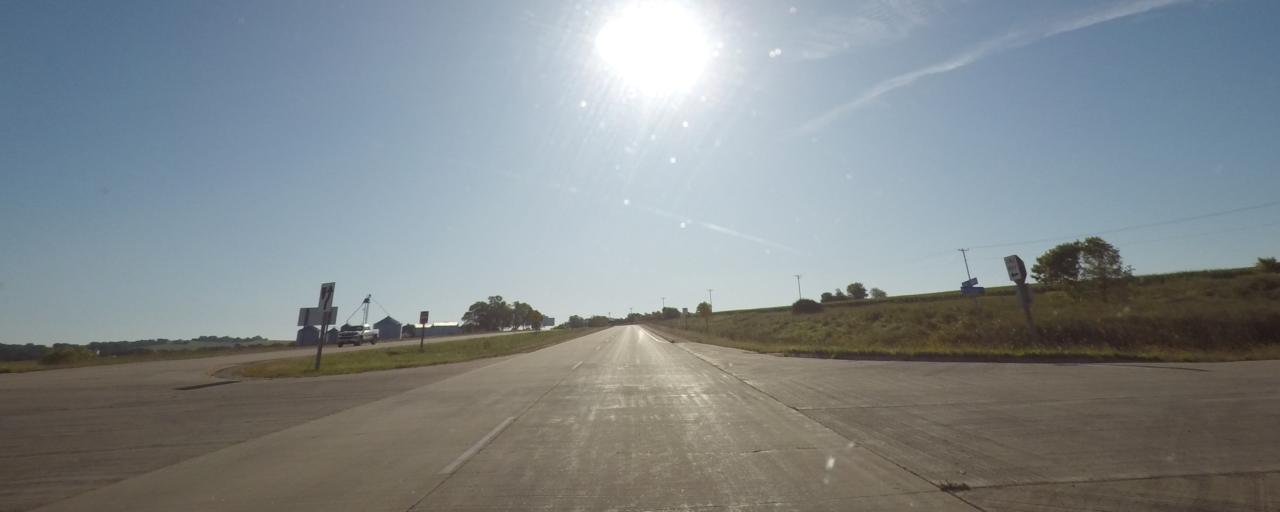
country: US
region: Wisconsin
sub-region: Dane County
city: Cottage Grove
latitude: 43.0293
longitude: -89.1890
